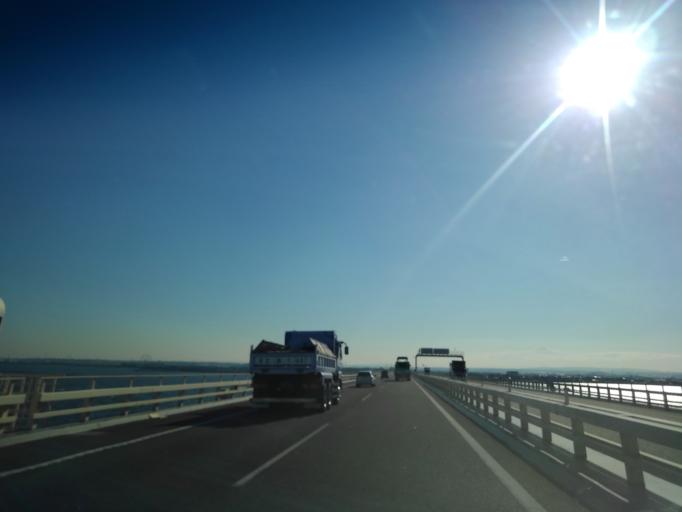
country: JP
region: Chiba
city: Kisarazu
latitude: 35.4442
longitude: 139.9040
